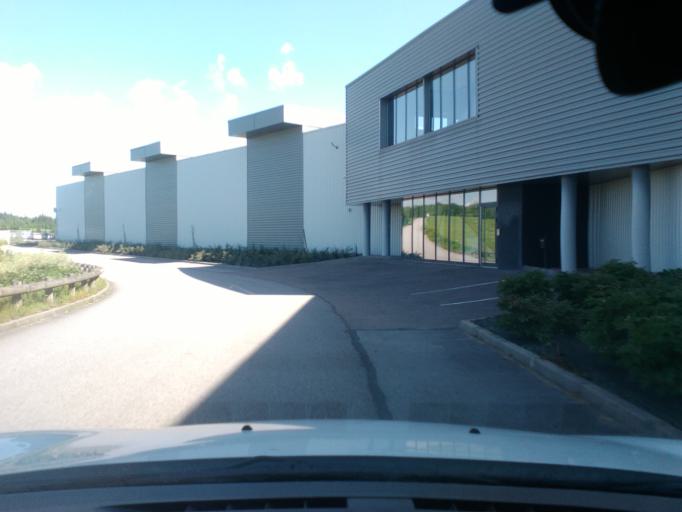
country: FR
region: Lorraine
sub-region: Departement des Vosges
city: Mirecourt
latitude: 48.3299
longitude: 6.1449
